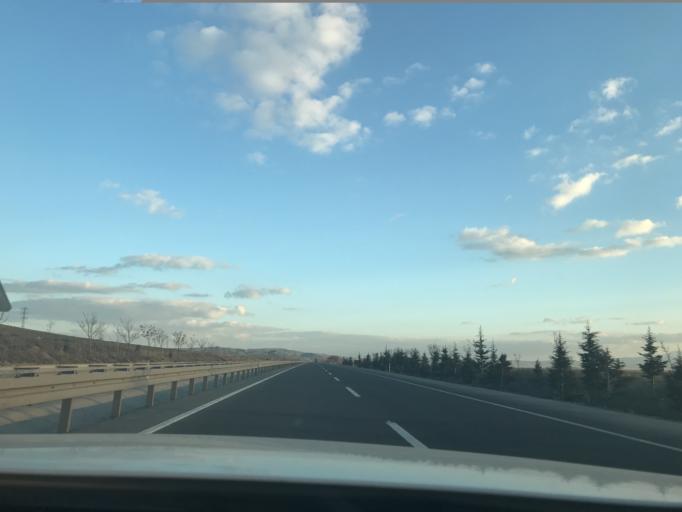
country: TR
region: Ankara
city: Yenice
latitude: 39.4039
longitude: 32.8734
